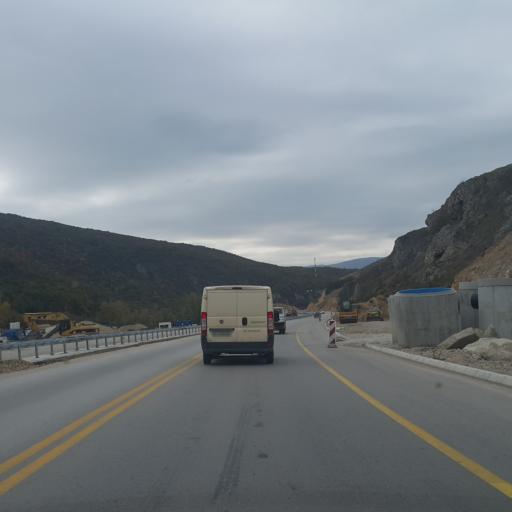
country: RS
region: Central Serbia
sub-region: Pirotski Okrug
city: Bela Palanka
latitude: 43.2233
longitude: 22.4269
